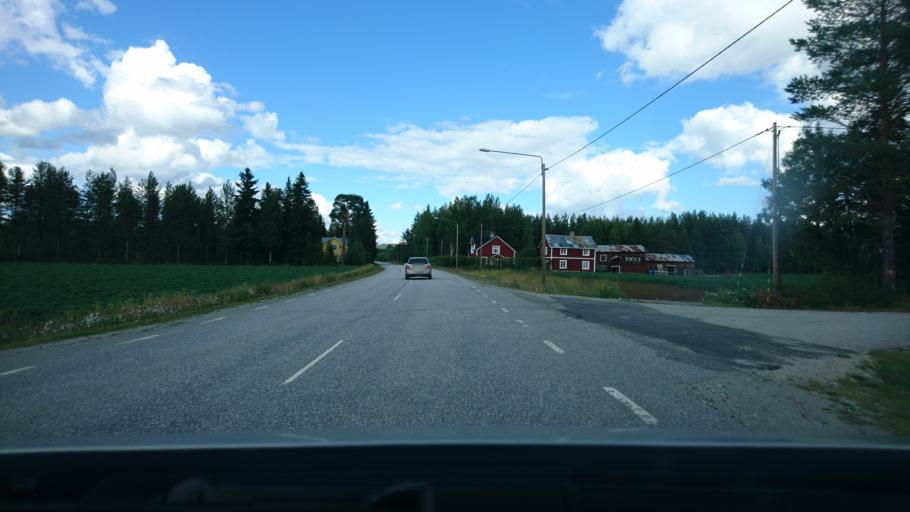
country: SE
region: Vaesterbotten
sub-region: Asele Kommun
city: Asele
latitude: 64.0114
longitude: 17.2896
